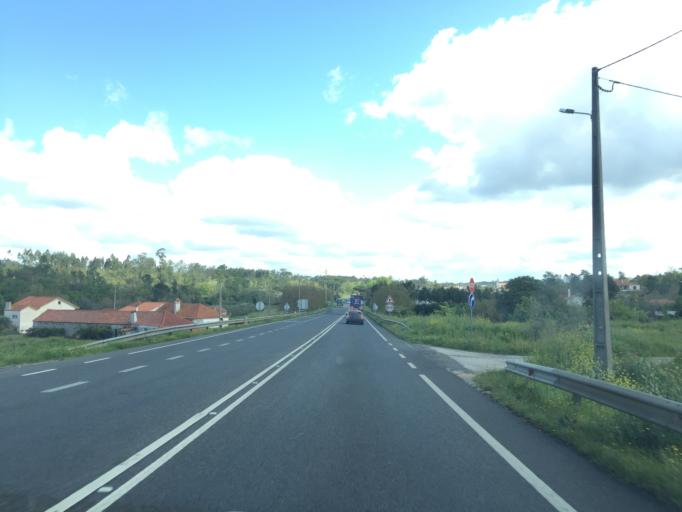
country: PT
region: Leiria
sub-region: Alcobaca
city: Aljubarrota
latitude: 39.5793
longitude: -8.8730
